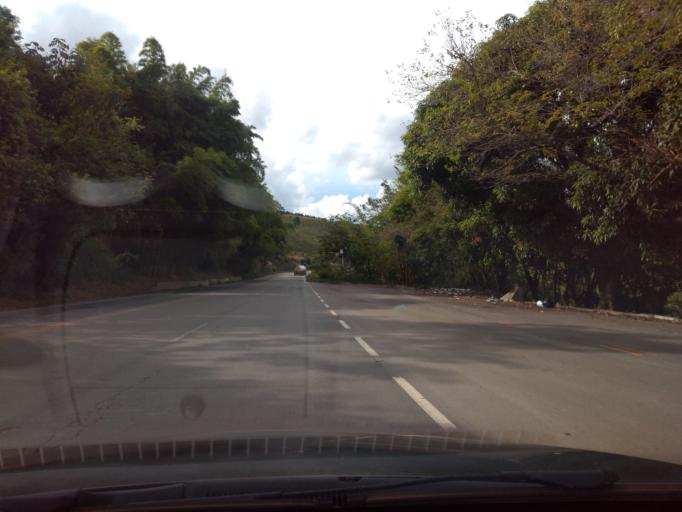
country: BR
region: Minas Gerais
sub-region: Varginha
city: Varginha
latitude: -21.6106
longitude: -45.4320
